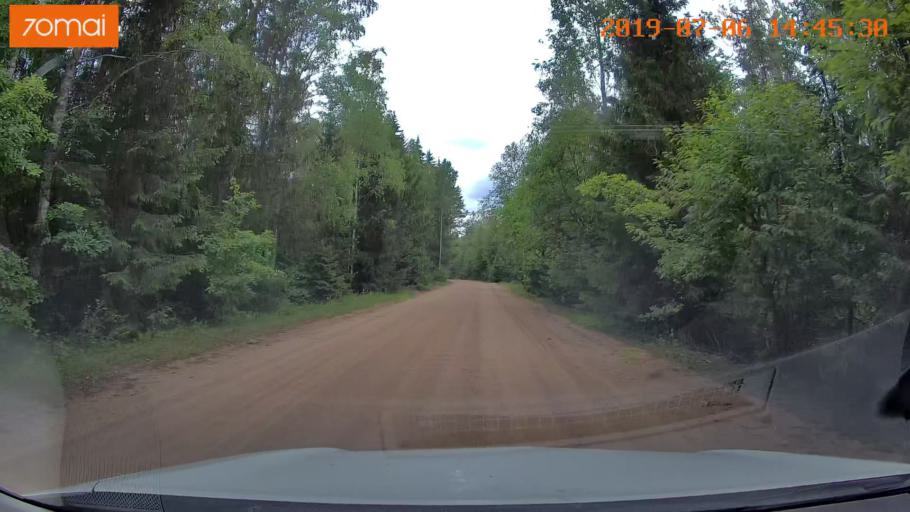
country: BY
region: Minsk
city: Ivyanyets
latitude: 53.9726
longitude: 26.6864
